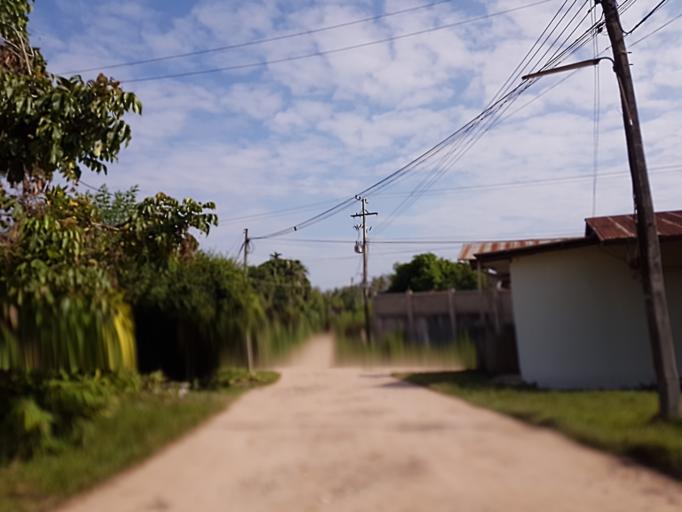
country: TH
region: Nong Khai
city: Tha Bo
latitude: 17.8661
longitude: 102.6078
